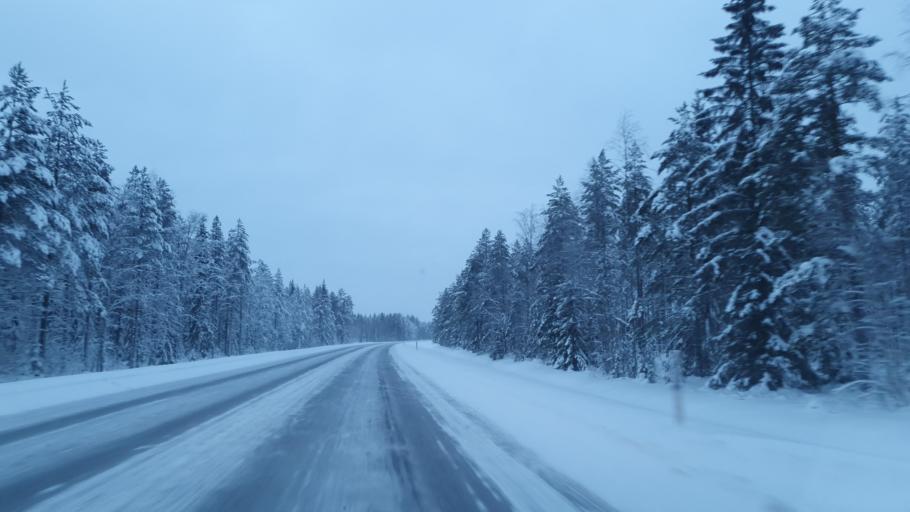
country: FI
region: Kainuu
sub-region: Kajaani
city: Vaala
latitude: 64.5980
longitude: 26.6925
